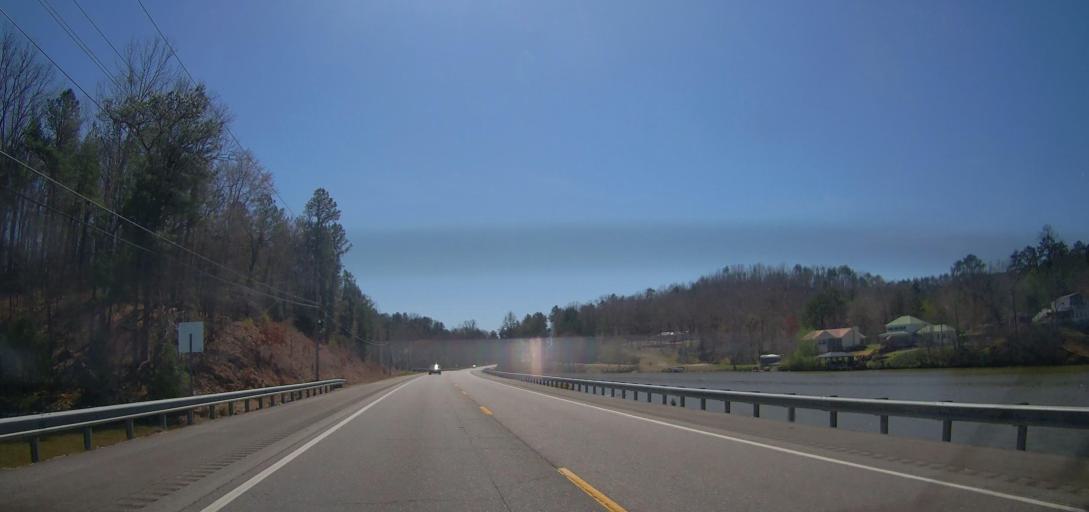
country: US
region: Alabama
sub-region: Calhoun County
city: Ohatchee
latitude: 33.8138
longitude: -86.0368
